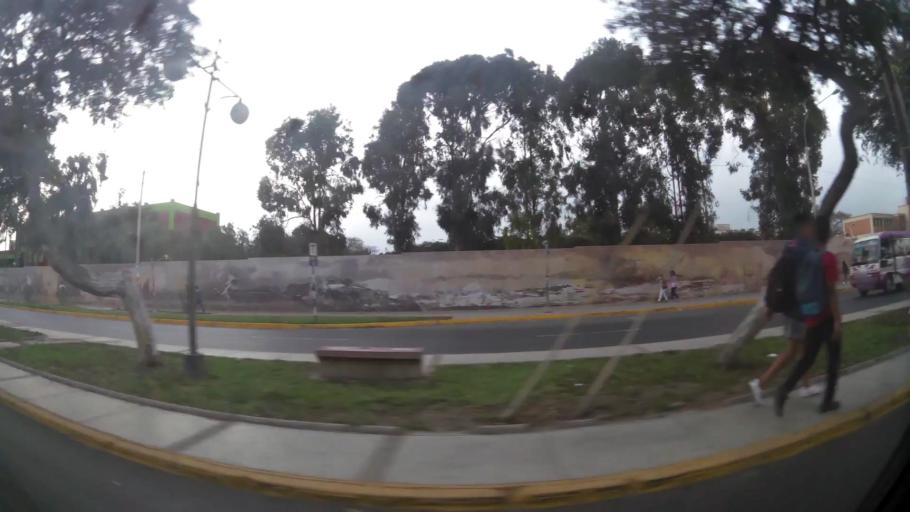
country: PE
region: La Libertad
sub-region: Provincia de Trujillo
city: Trujillo
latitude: -8.1143
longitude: -79.0358
